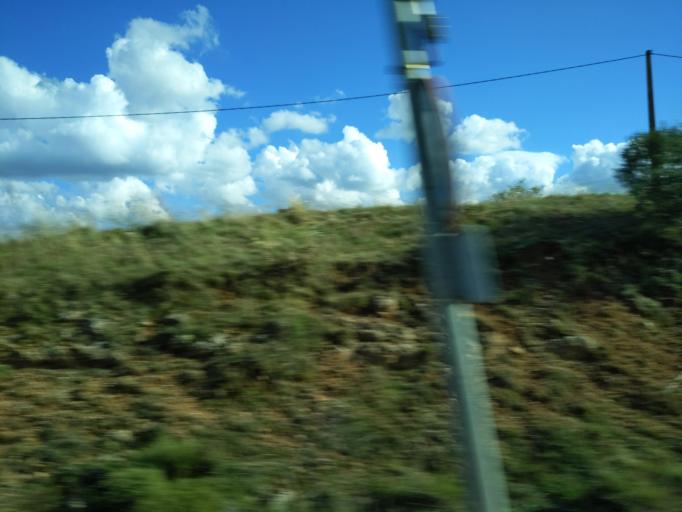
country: ES
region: Castille and Leon
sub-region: Provincia de Soria
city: Soria
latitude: 41.7527
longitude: -2.4805
